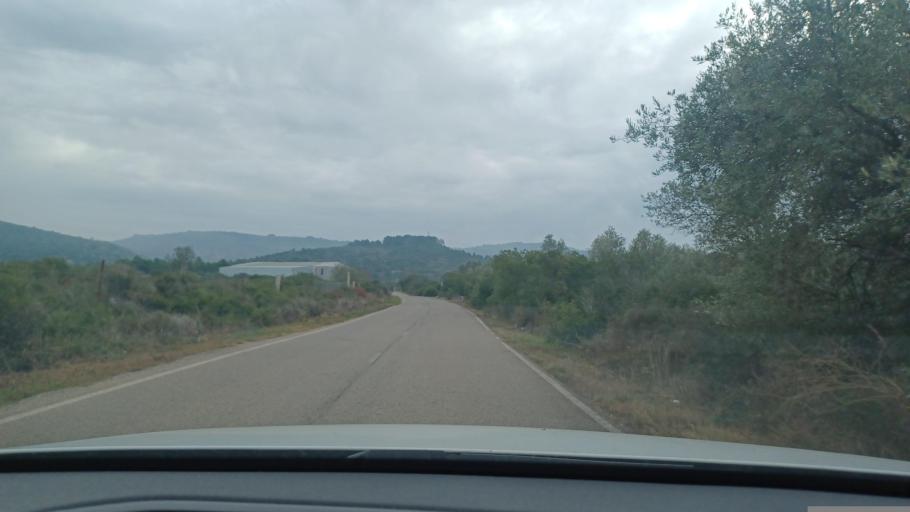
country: ES
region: Catalonia
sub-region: Provincia de Tarragona
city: Santa Barbara
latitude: 40.6625
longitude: 0.4598
